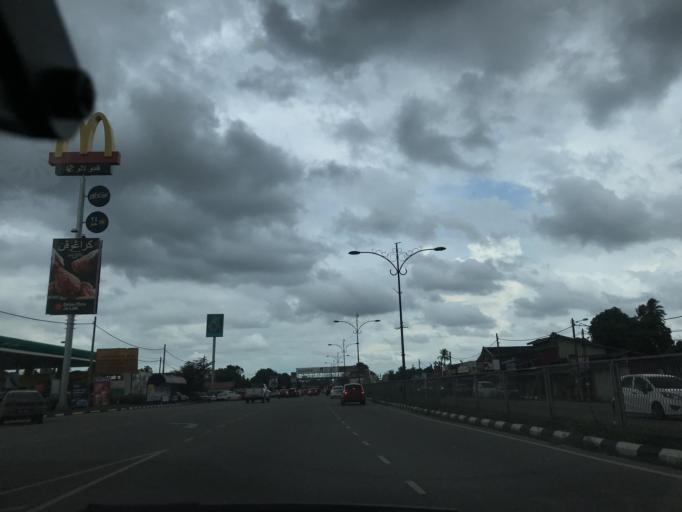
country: MY
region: Kelantan
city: Kota Bharu
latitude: 6.1189
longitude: 102.2179
